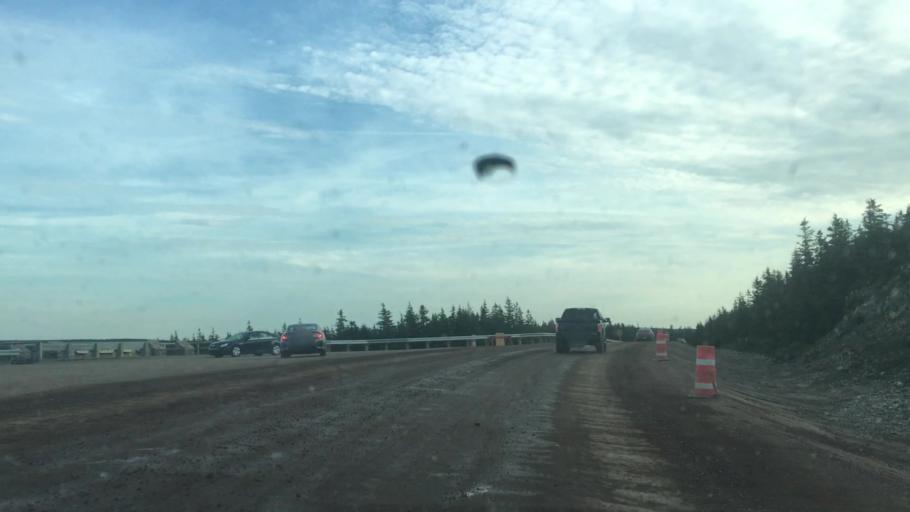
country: CA
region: Nova Scotia
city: Sydney Mines
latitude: 46.8037
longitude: -60.8435
